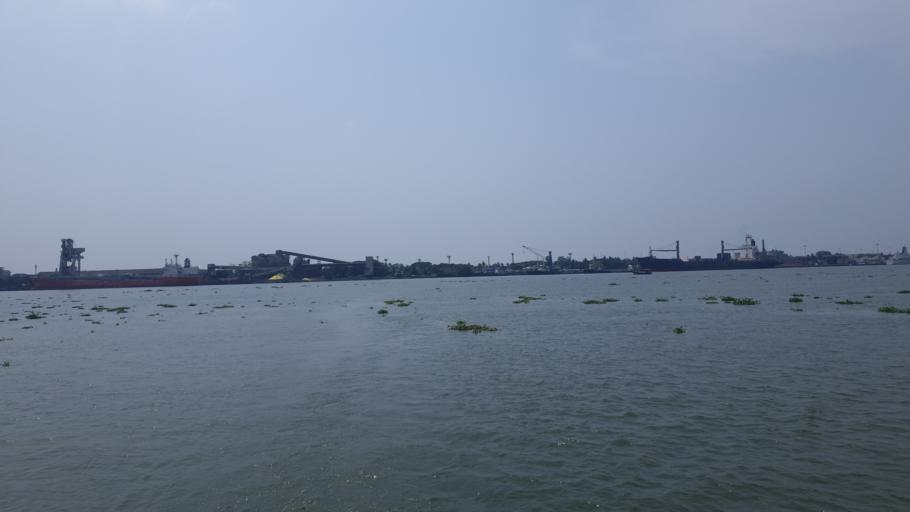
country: IN
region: Kerala
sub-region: Ernakulam
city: Cochin
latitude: 9.9714
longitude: 76.2763
